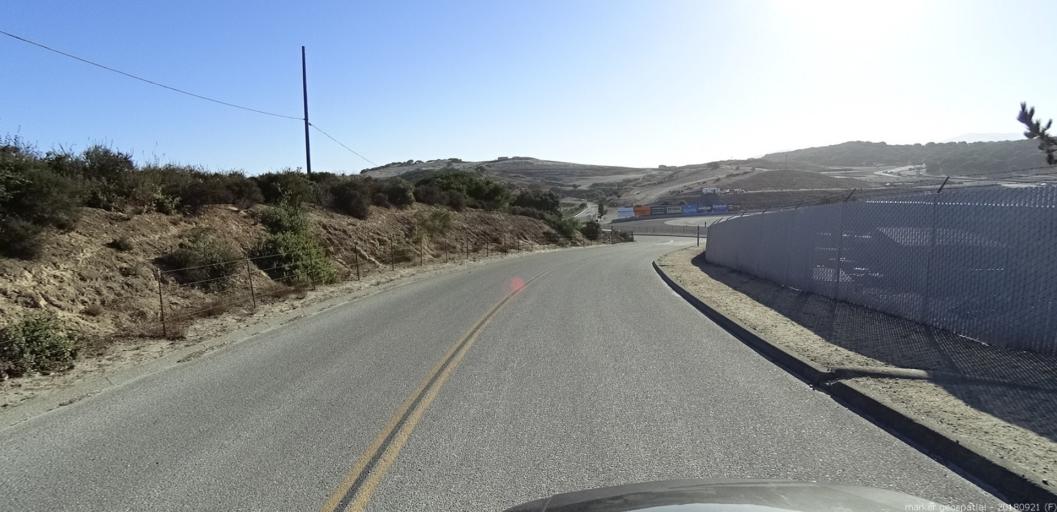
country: US
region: California
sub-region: Monterey County
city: Del Rey Oaks
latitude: 36.5890
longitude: -121.7566
